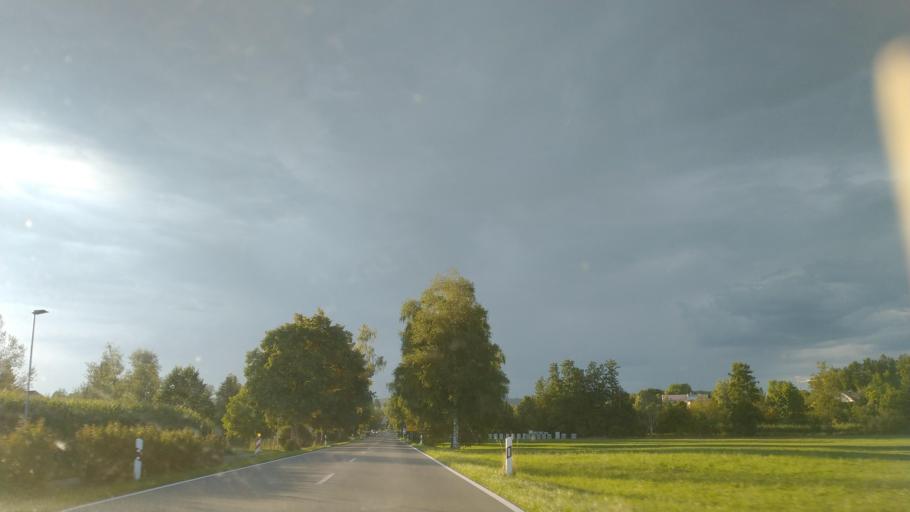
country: DE
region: Baden-Wuerttemberg
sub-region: Tuebingen Region
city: Amtzell
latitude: 47.7011
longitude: 9.7532
